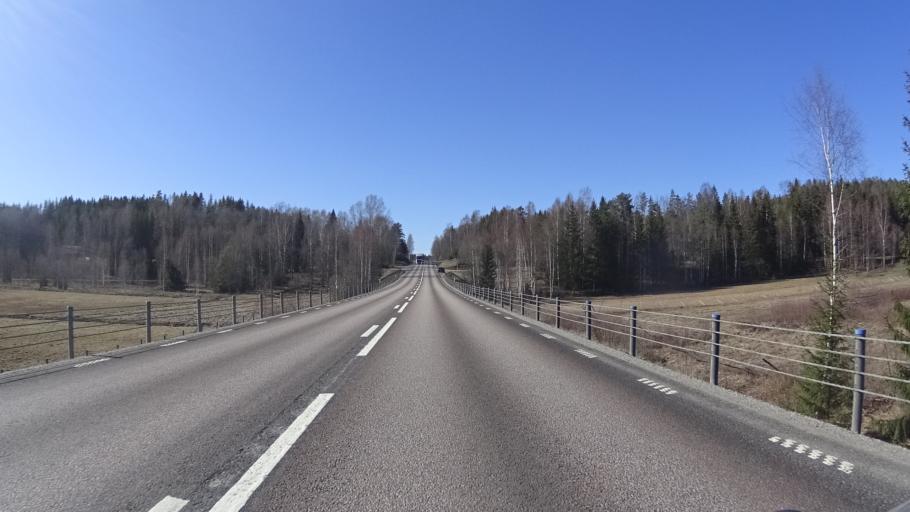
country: SE
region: Vaermland
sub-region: Sunne Kommun
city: Sunne
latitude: 59.6629
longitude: 12.9225
